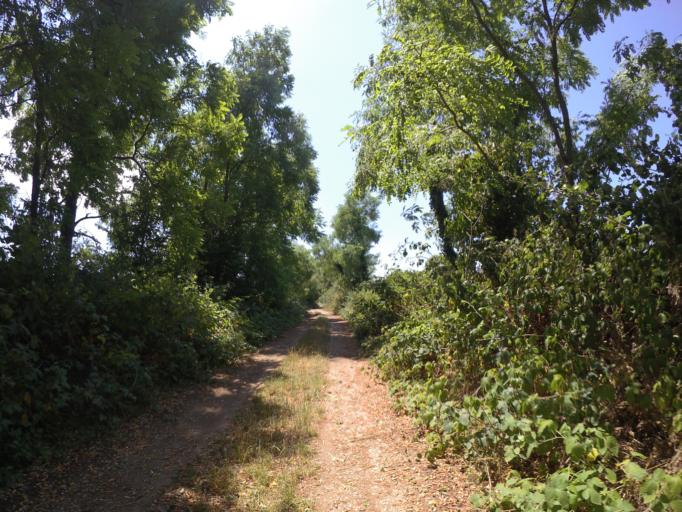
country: IT
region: Friuli Venezia Giulia
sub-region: Provincia di Udine
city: Talmassons
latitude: 45.9378
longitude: 13.1025
